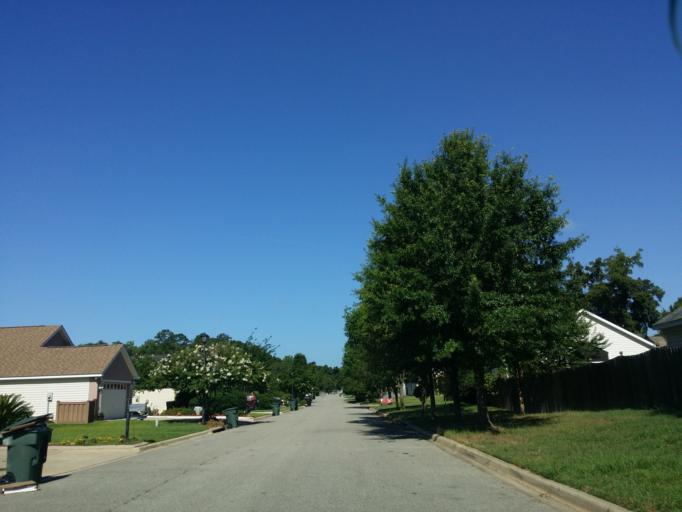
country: US
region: Florida
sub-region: Leon County
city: Tallahassee
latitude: 30.4563
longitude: -84.2166
